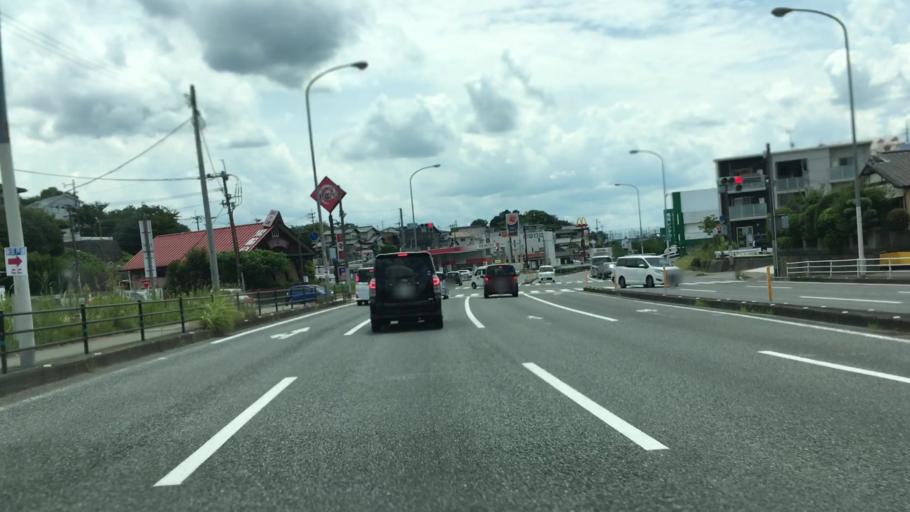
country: JP
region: Fukuoka
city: Dazaifu
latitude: 33.5038
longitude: 130.5309
